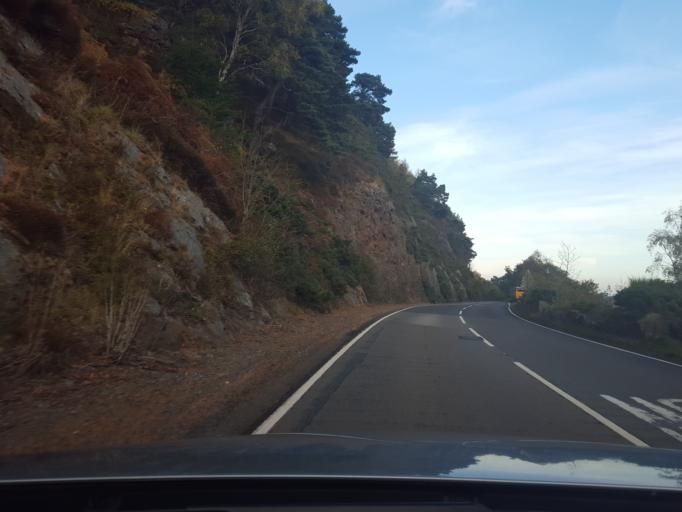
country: GB
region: Scotland
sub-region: Highland
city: Beauly
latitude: 57.3517
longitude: -4.4086
